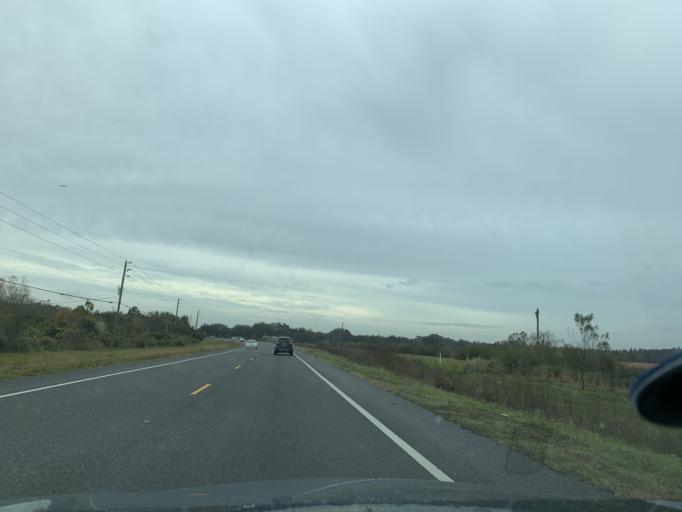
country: US
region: Florida
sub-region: Pasco County
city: Zephyrhills West
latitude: 28.2329
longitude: -82.2468
